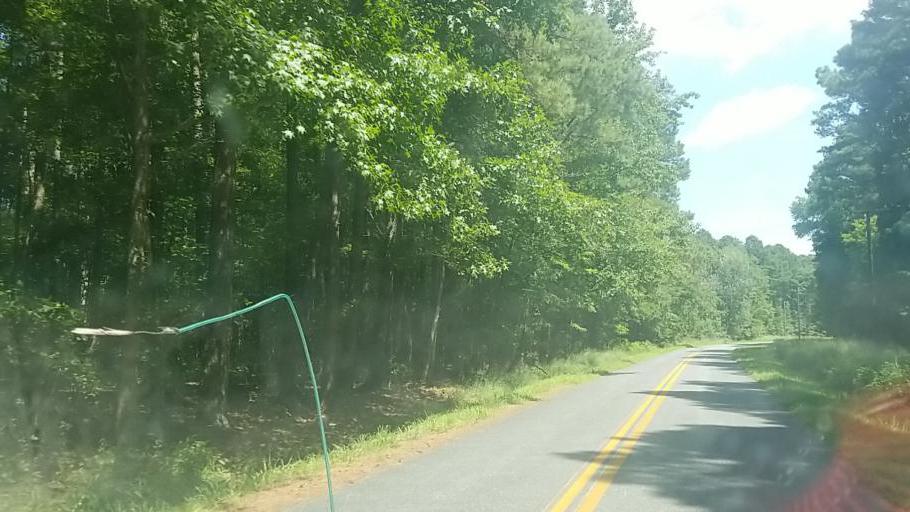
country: US
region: Maryland
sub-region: Wicomico County
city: Hebron
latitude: 38.4266
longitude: -75.8784
